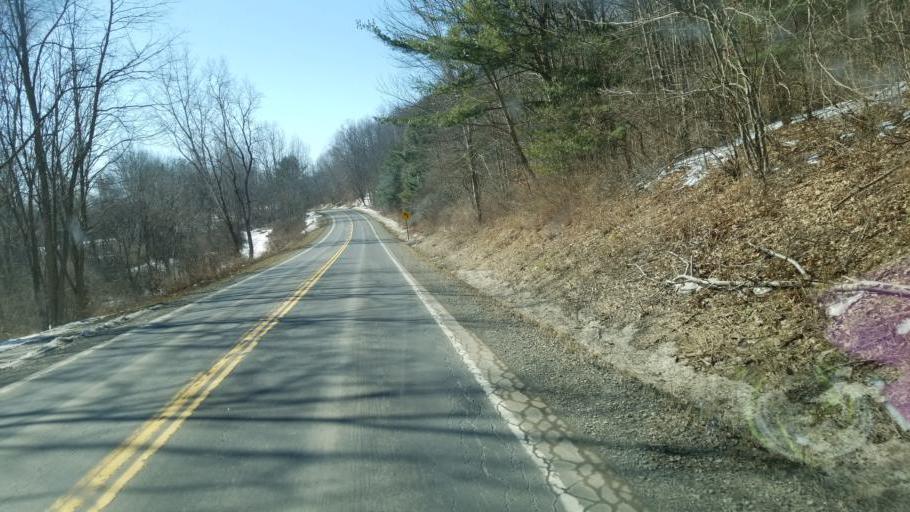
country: US
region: New York
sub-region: Steuben County
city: Hornell
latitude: 42.3470
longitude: -77.7199
